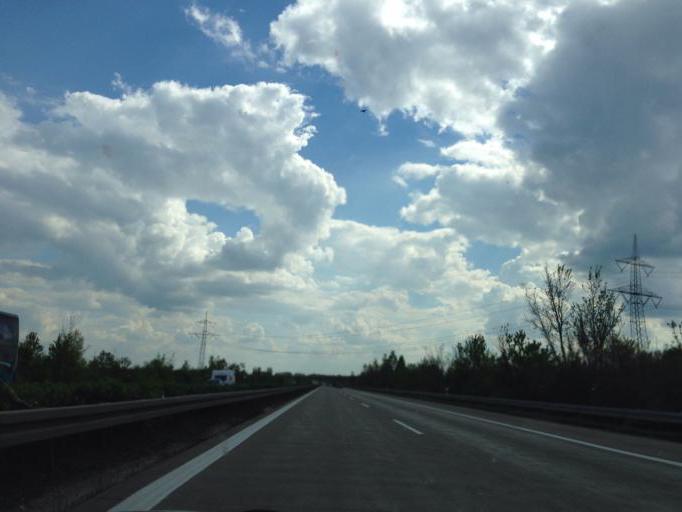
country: DE
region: Saxony-Anhalt
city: Biere
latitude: 51.9841
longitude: 11.6678
